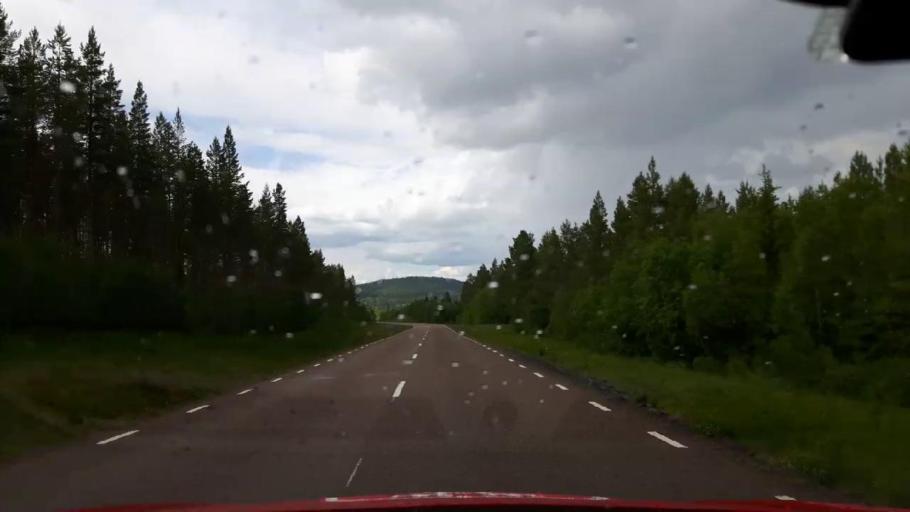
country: SE
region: Jaemtland
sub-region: Krokoms Kommun
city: Valla
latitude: 63.8938
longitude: 14.2611
